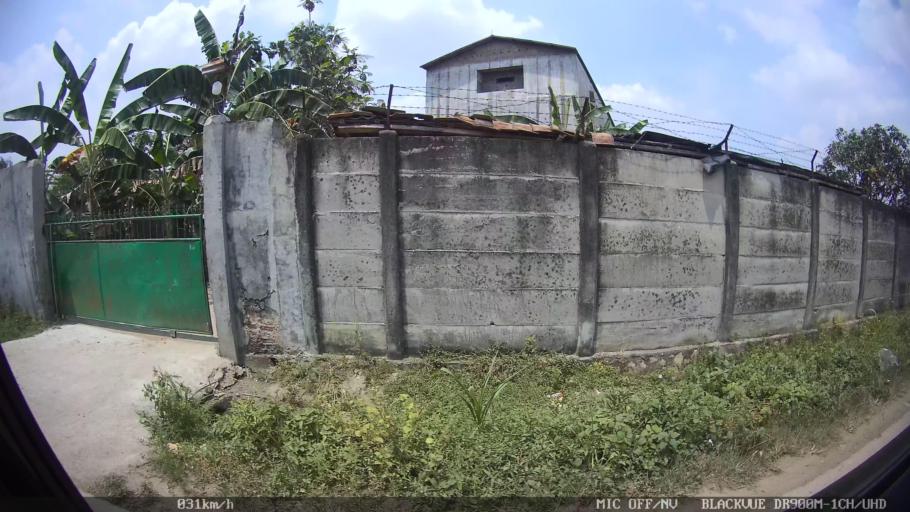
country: ID
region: Lampung
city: Pringsewu
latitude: -5.3544
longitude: 104.9931
